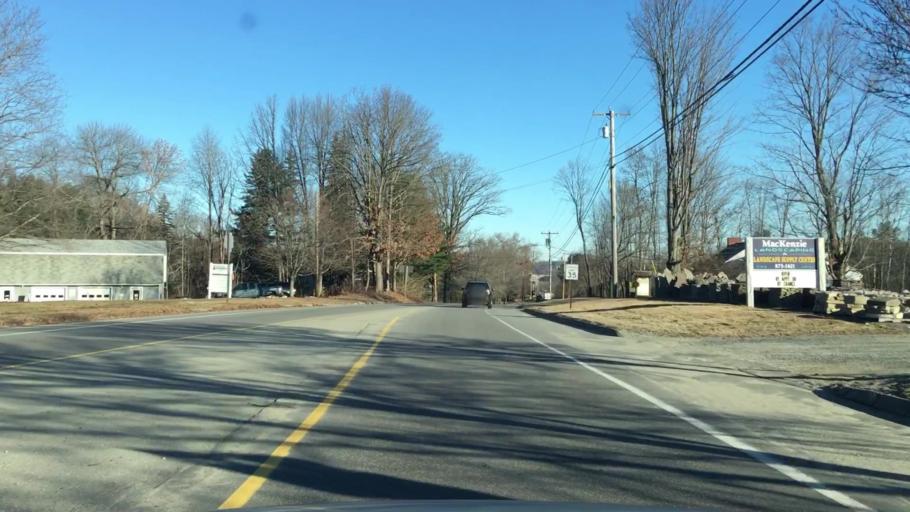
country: US
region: Maine
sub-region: Kennebec County
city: Waterville
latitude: 44.5288
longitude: -69.6402
